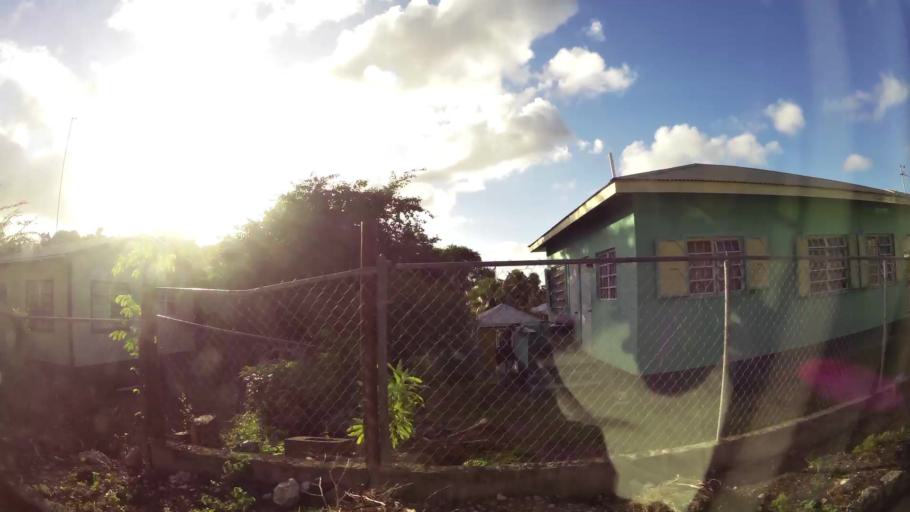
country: AG
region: Saint George
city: Piggotts
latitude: 17.1269
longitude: -61.8019
